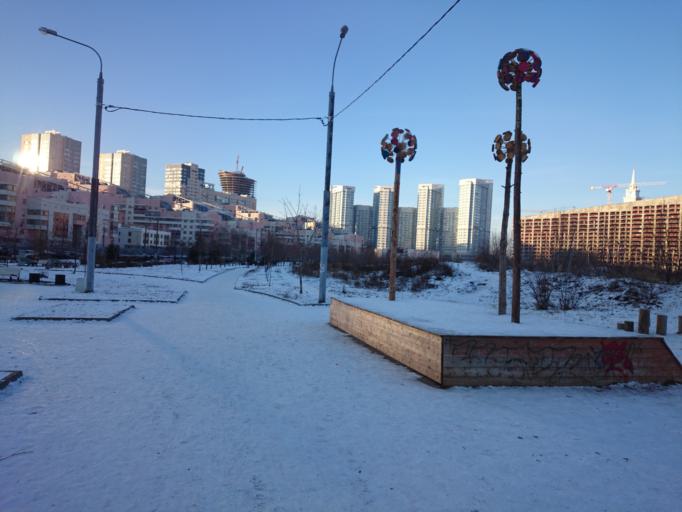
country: RU
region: Moscow
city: Sokol
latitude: 55.7860
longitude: 37.5266
